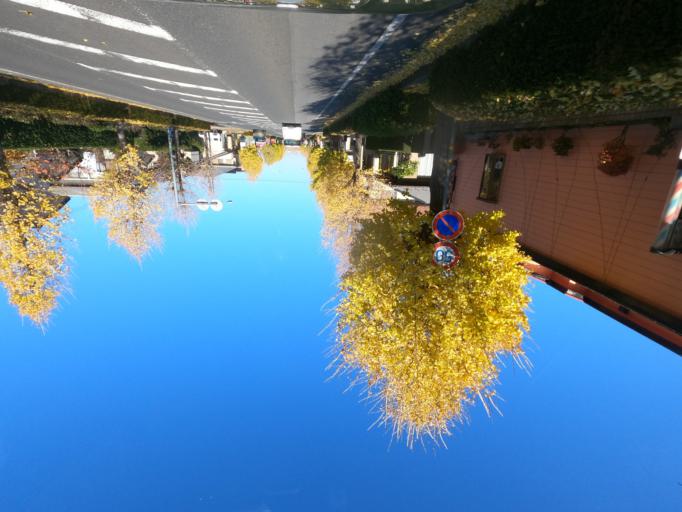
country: JP
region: Ibaraki
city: Mitsukaido
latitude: 35.9720
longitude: 139.9709
